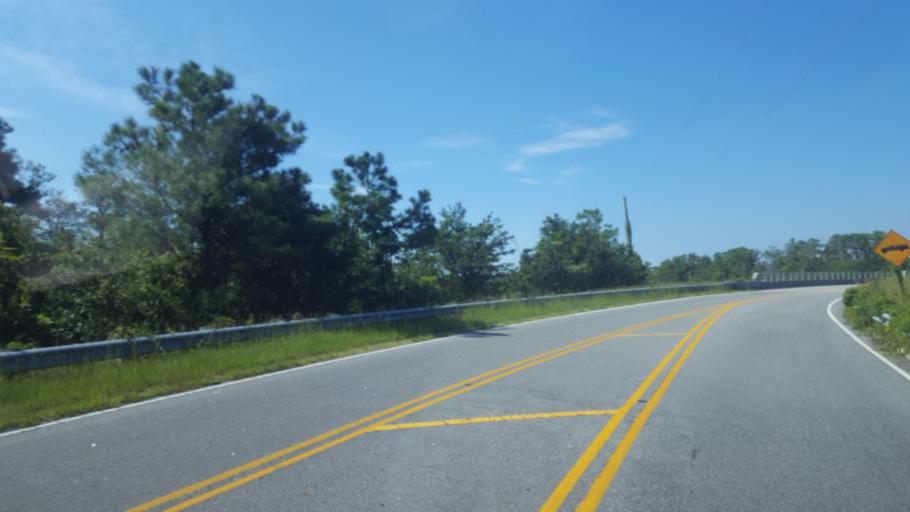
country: US
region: North Carolina
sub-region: Dare County
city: Kill Devil Hills
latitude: 36.0099
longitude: -75.6993
